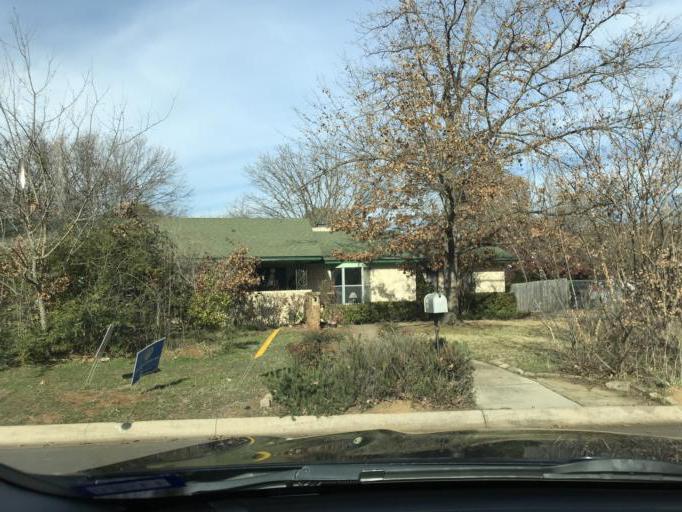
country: US
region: Texas
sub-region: Denton County
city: Denton
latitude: 33.2333
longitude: -97.1461
